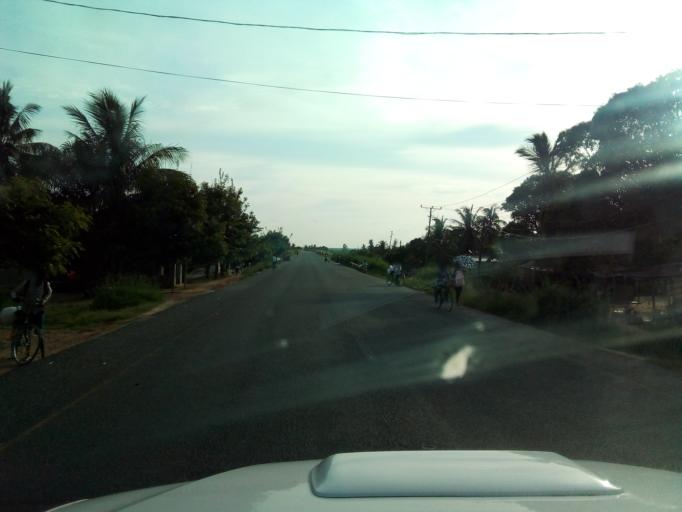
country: MZ
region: Zambezia
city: Quelimane
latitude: -17.4908
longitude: 37.0273
